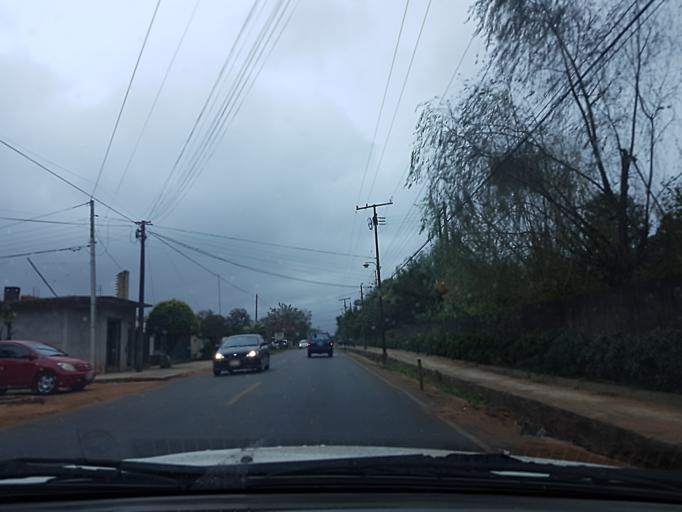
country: PY
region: Central
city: Limpio
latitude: -25.2497
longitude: -57.5029
